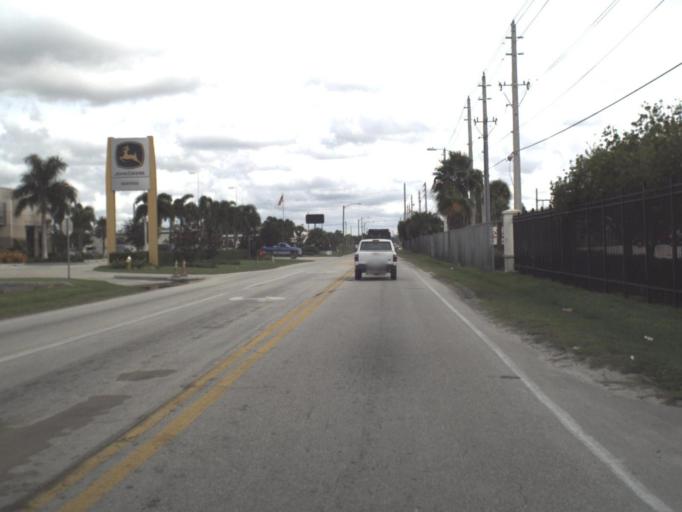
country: US
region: Florida
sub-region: Lee County
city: Fort Myers
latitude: 26.6229
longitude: -81.8518
